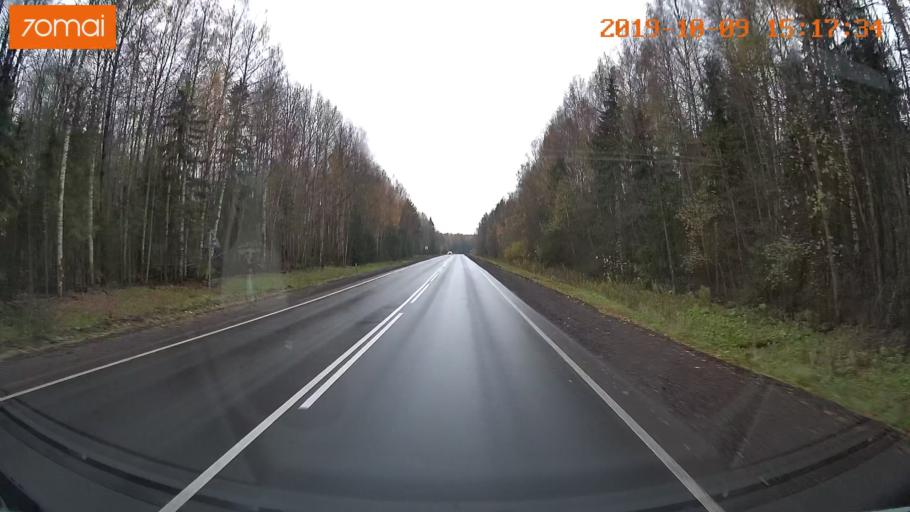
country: RU
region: Kostroma
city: Susanino
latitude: 58.0967
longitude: 41.5823
